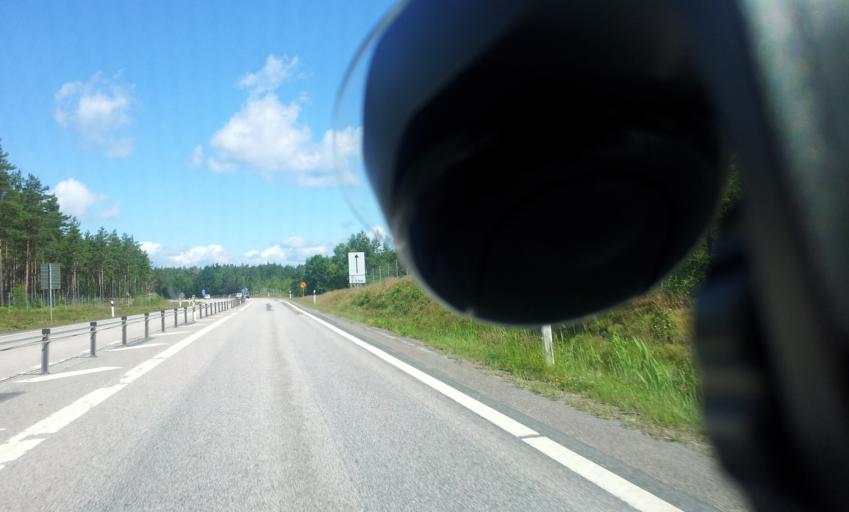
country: SE
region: Kalmar
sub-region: Oskarshamns Kommun
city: Paskallavik
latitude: 57.1107
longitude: 16.4991
